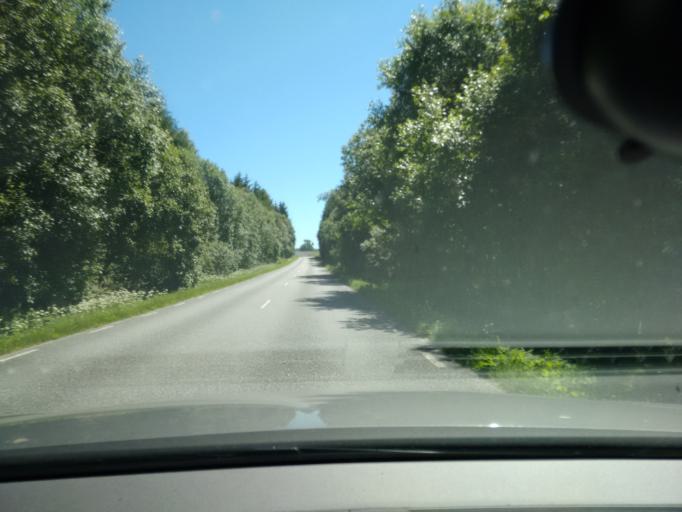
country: SE
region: Skane
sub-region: Kristianstads Kommun
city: Degeberga
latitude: 55.7832
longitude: 13.8767
